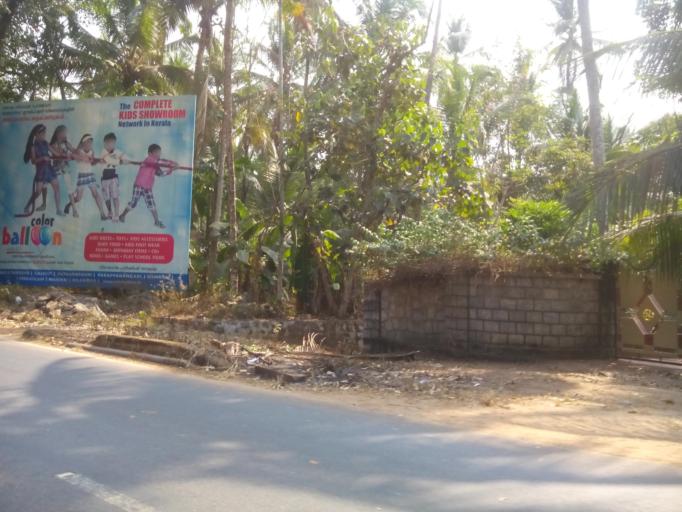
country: IN
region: Kerala
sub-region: Kozhikode
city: Naduvannur
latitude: 11.5733
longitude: 75.7532
